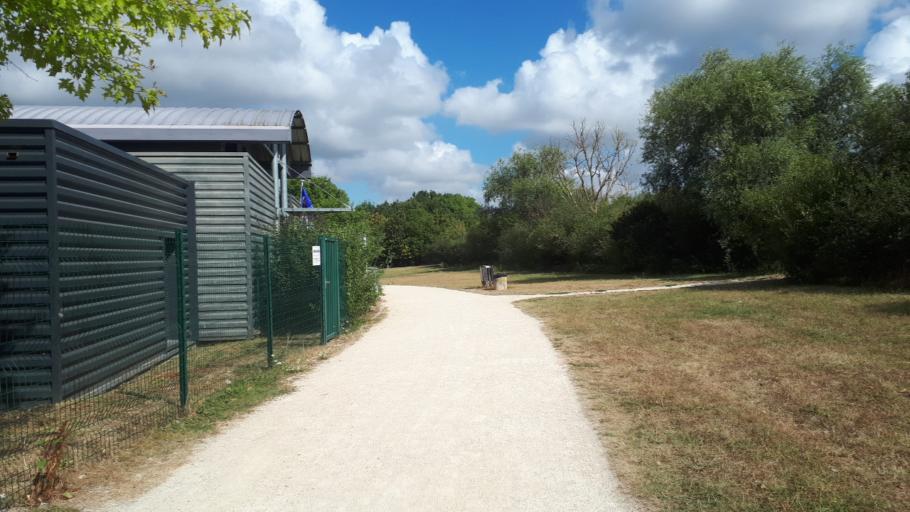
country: FR
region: Centre
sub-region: Departement du Loir-et-Cher
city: Villiers-sur-Loir
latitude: 47.7963
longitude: 0.9948
